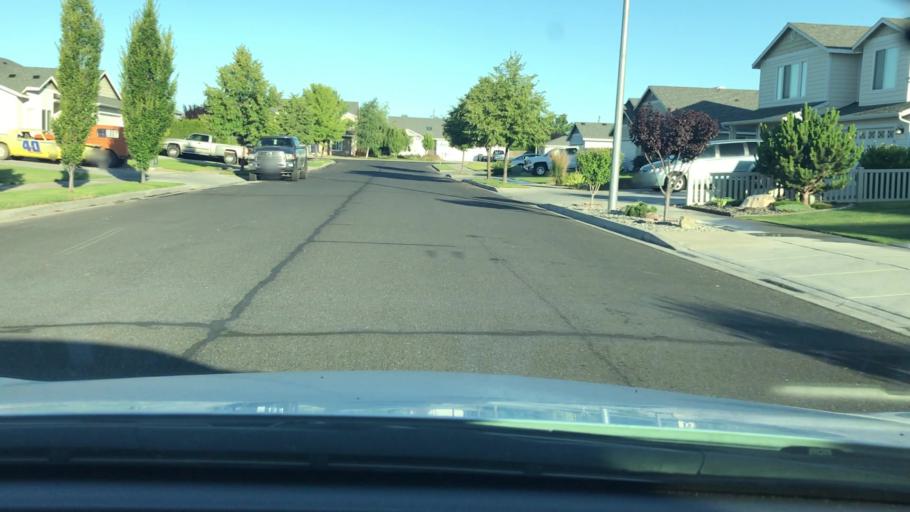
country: US
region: Washington
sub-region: Grant County
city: Moses Lake
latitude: 47.1207
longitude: -119.2545
